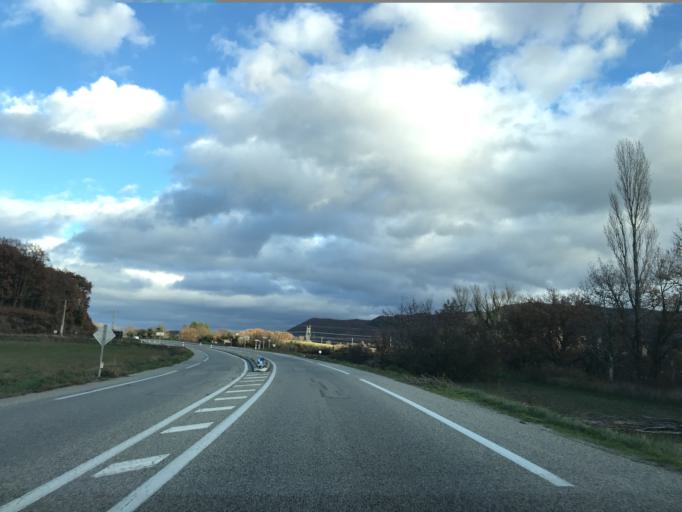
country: FR
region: Rhone-Alpes
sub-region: Departement de l'Ardeche
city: Saint-Julien-en-Saint-Alban
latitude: 44.7092
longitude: 4.7197
